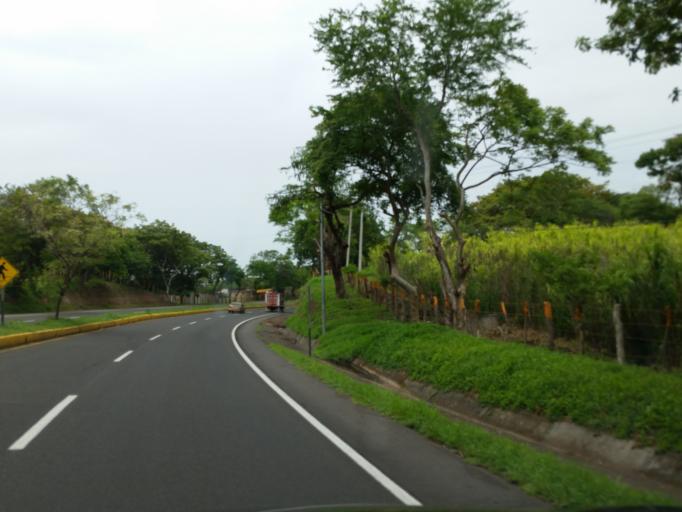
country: NI
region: Granada
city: Granada
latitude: 11.9618
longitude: -85.9956
